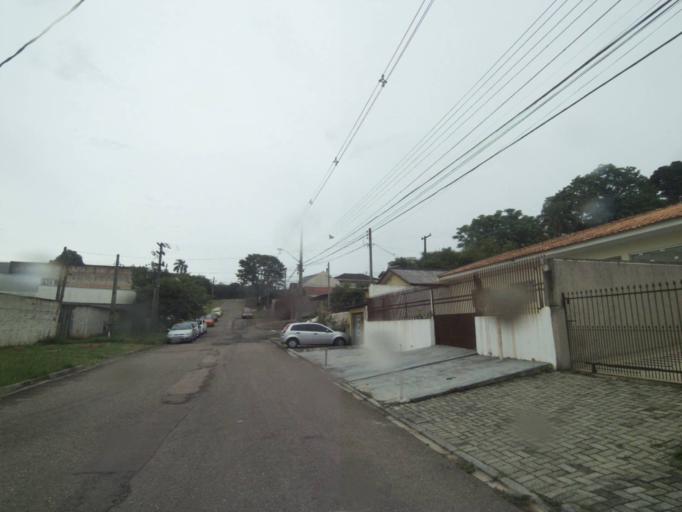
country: BR
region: Parana
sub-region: Curitiba
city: Curitiba
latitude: -25.4297
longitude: -49.3289
